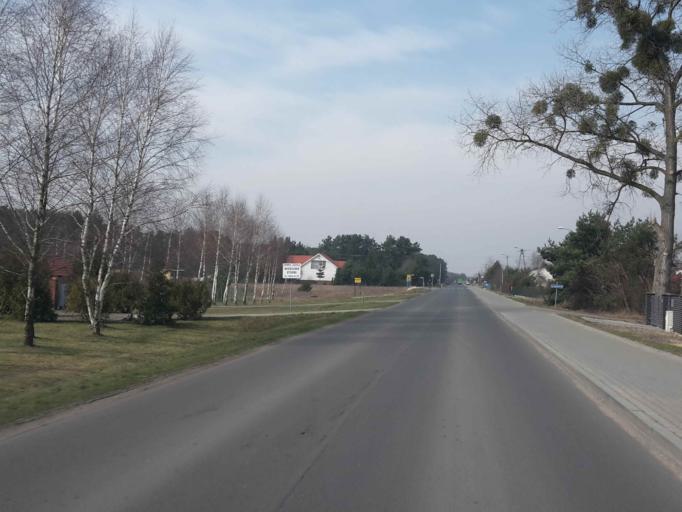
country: PL
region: Kujawsko-Pomorskie
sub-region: Powiat nakielski
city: Szubin
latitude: 53.0749
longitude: 17.8040
